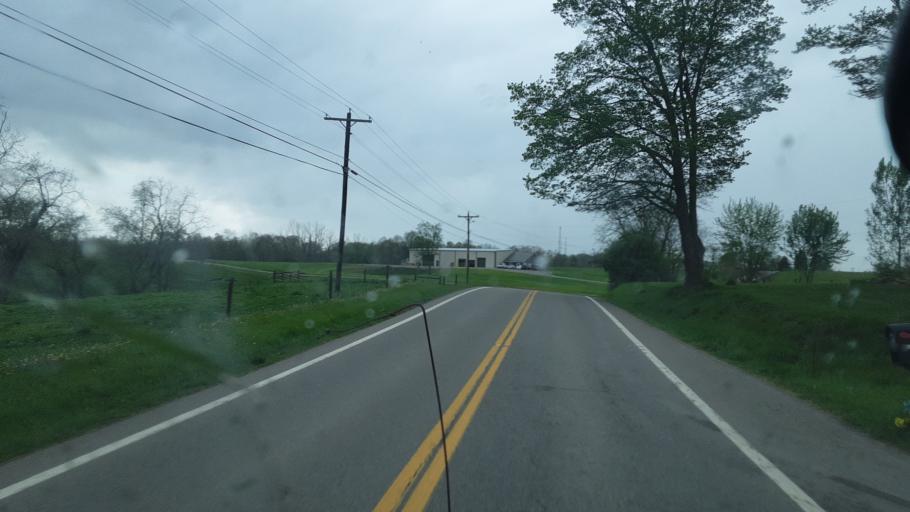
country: US
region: Ohio
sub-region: Muskingum County
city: New Concord
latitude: 39.9703
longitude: -81.7199
